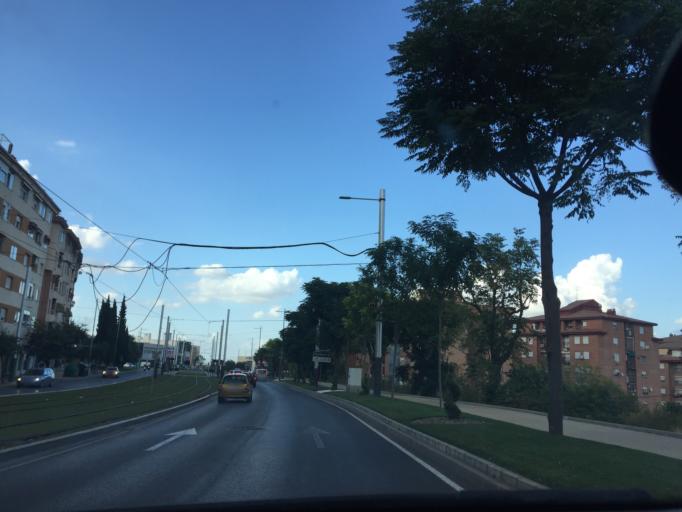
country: ES
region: Andalusia
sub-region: Provincia de Jaen
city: Jaen
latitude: 37.7818
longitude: -3.7835
